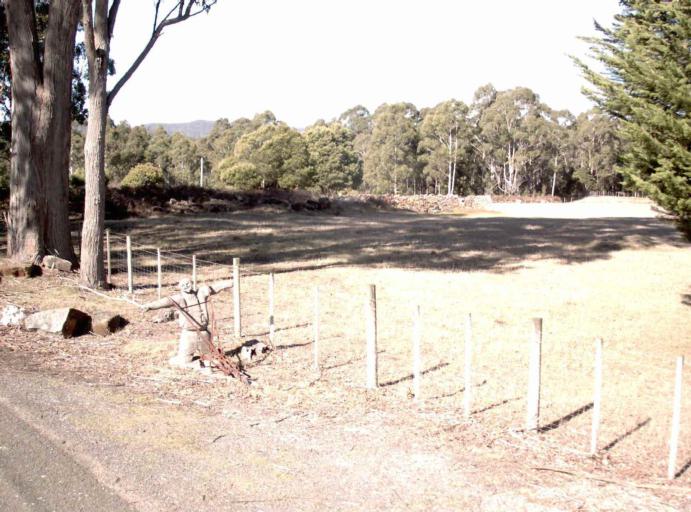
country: AU
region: Tasmania
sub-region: Launceston
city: Mayfield
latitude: -41.3121
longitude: 147.2016
